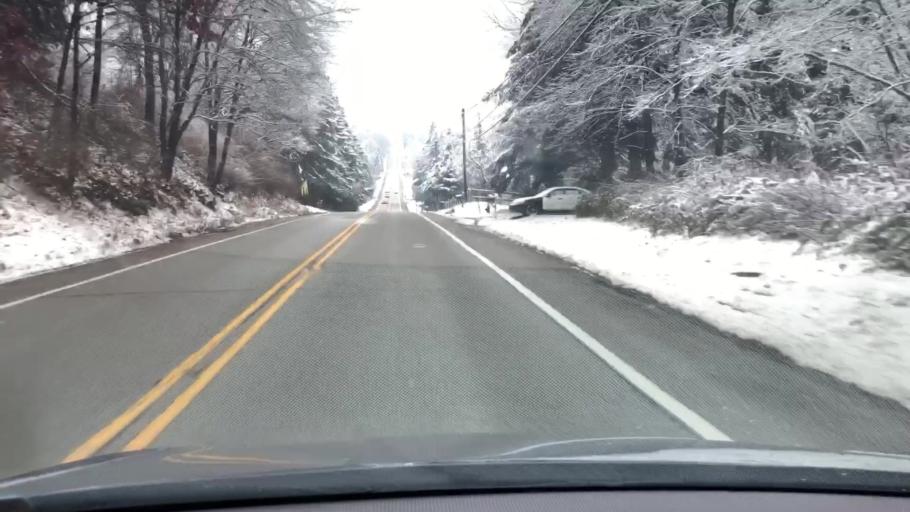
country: US
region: Pennsylvania
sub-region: Fayette County
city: Hopwood
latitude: 39.8270
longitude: -79.5960
